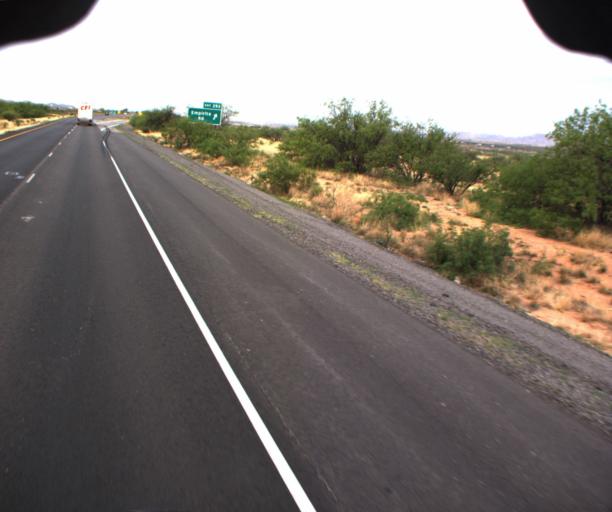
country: US
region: Arizona
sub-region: Cochise County
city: Mescal
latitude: 31.9754
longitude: -110.5051
